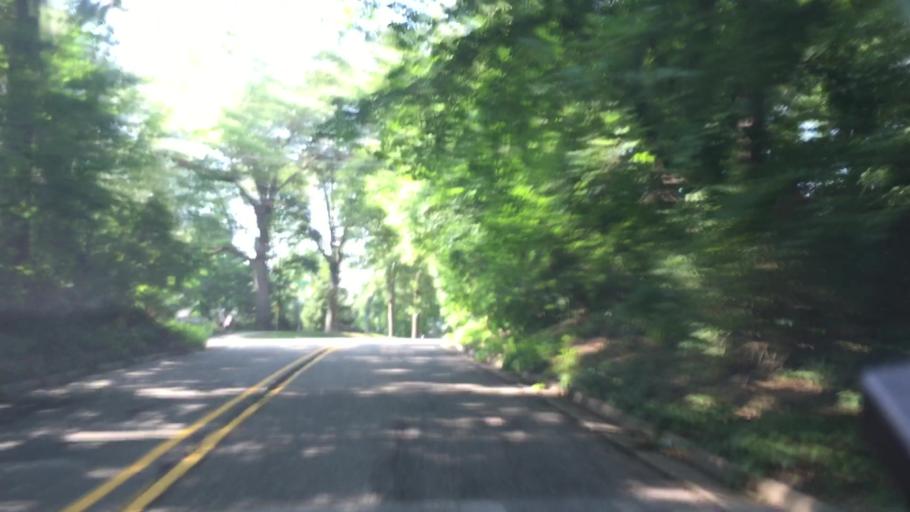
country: US
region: Michigan
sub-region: Oakland County
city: Franklin
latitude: 42.5374
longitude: -83.2964
